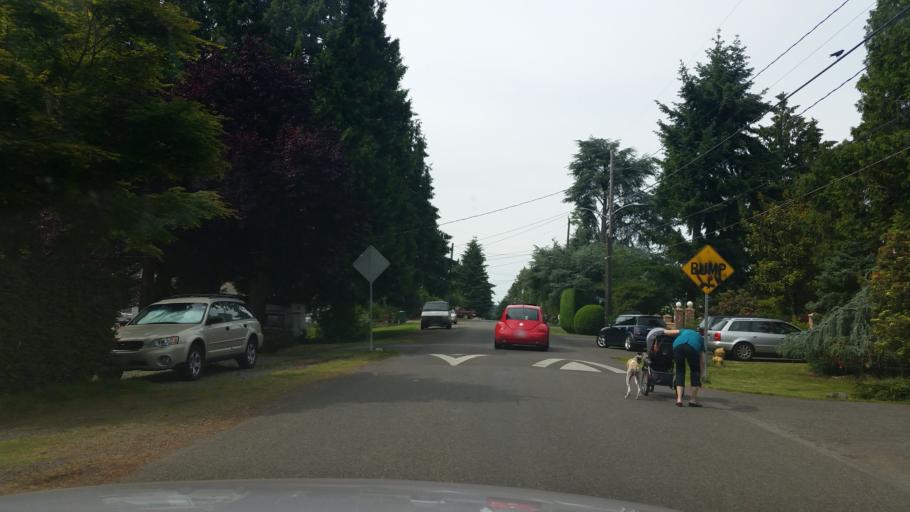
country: US
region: Washington
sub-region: King County
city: Lake Forest Park
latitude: 47.7306
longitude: -122.2884
